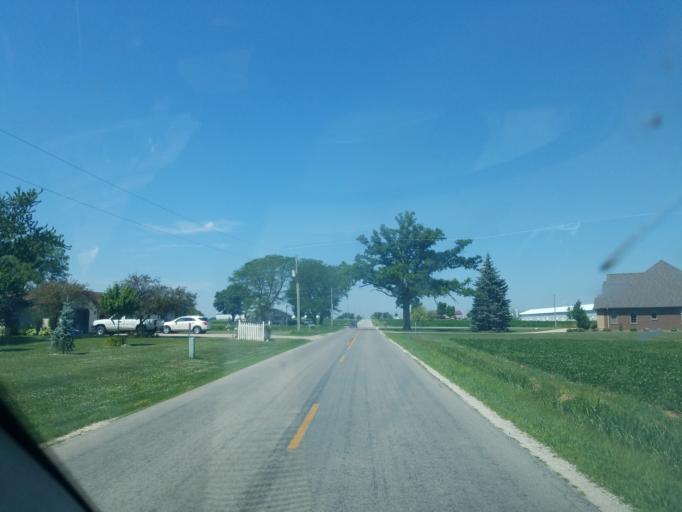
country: US
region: Ohio
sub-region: Mercer County
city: Saint Henry
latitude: 40.4506
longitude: -84.6658
